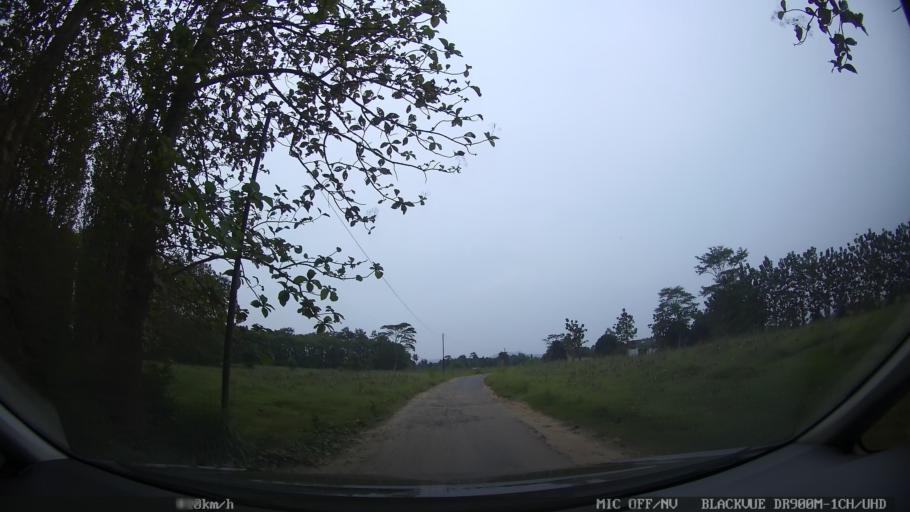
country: ID
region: Lampung
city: Panjang
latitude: -5.4071
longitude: 105.3574
